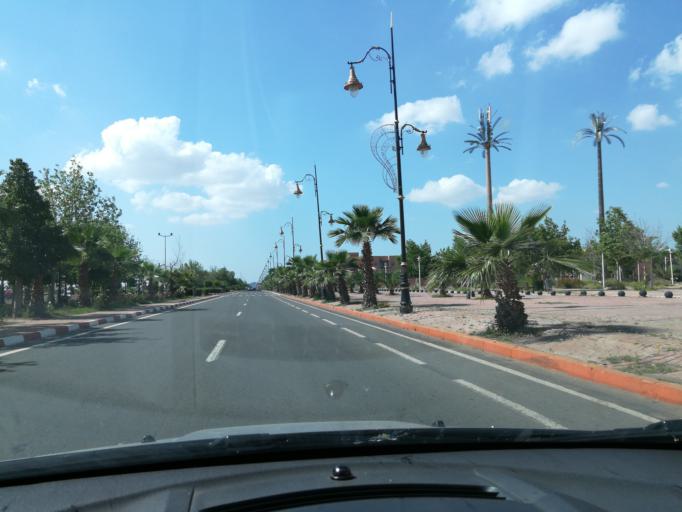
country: MA
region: Marrakech-Tensift-Al Haouz
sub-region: Marrakech
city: Marrakesh
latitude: 31.5911
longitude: -7.9904
